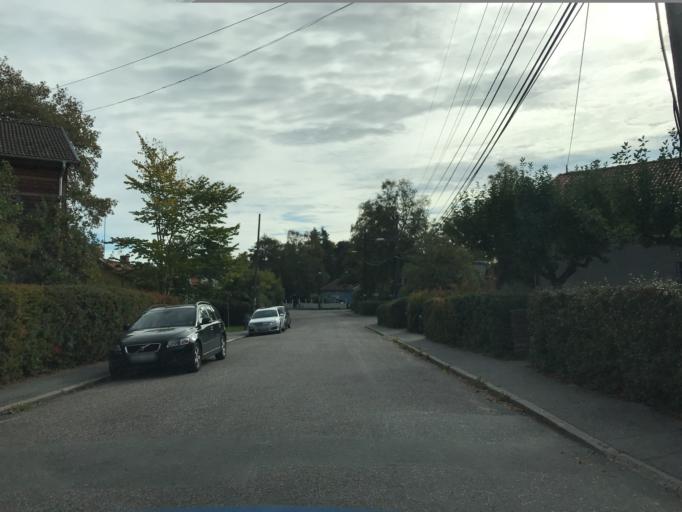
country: SE
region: Stockholm
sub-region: Huddinge Kommun
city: Huddinge
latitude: 59.2740
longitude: 17.9759
